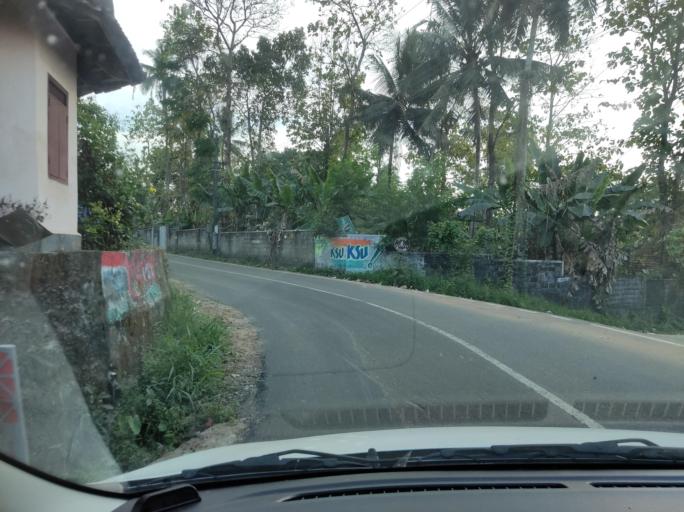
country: IN
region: Kerala
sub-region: Kottayam
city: Kottayam
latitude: 9.6469
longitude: 76.5183
